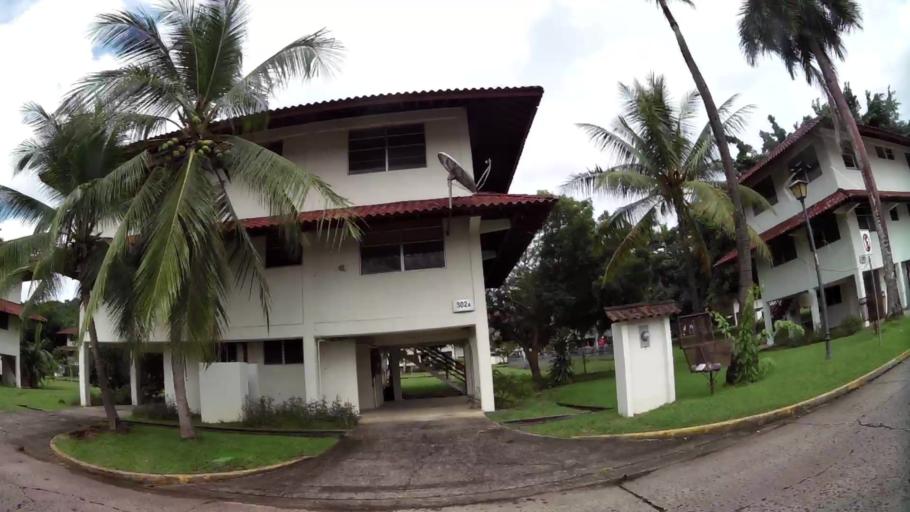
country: PA
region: Panama
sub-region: Distrito de Panama
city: Ancon
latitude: 9.0028
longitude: -79.5820
